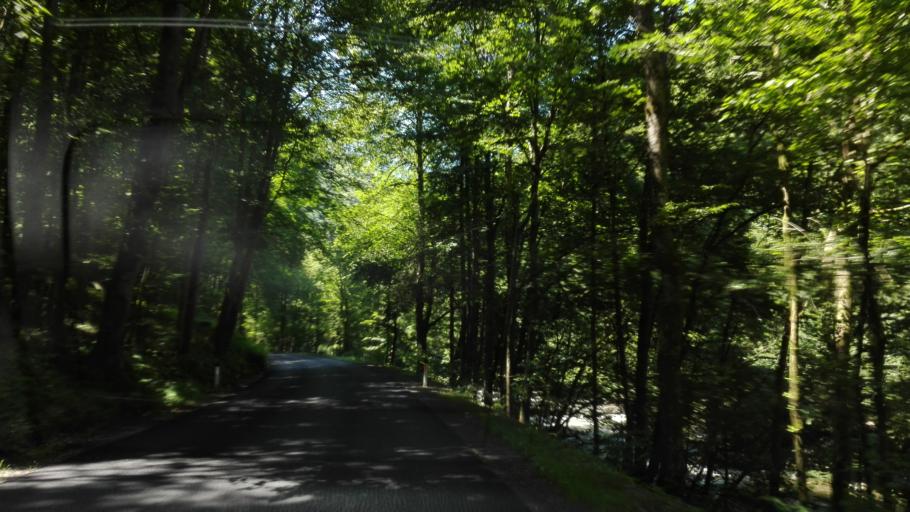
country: AT
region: Upper Austria
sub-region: Politischer Bezirk Rohrbach
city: Kleinzell im Muehlkreis
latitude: 48.3766
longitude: 13.9374
